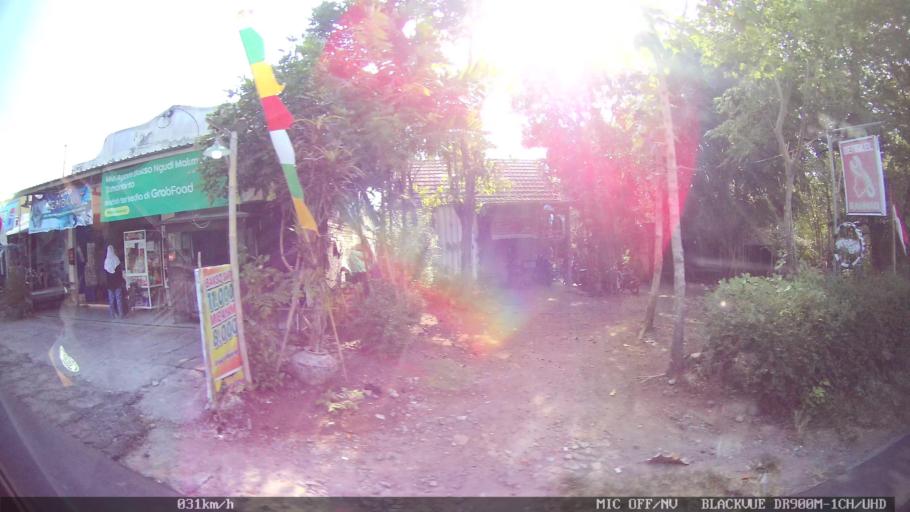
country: ID
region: Daerah Istimewa Yogyakarta
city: Kasihan
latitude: -7.8327
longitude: 110.3234
